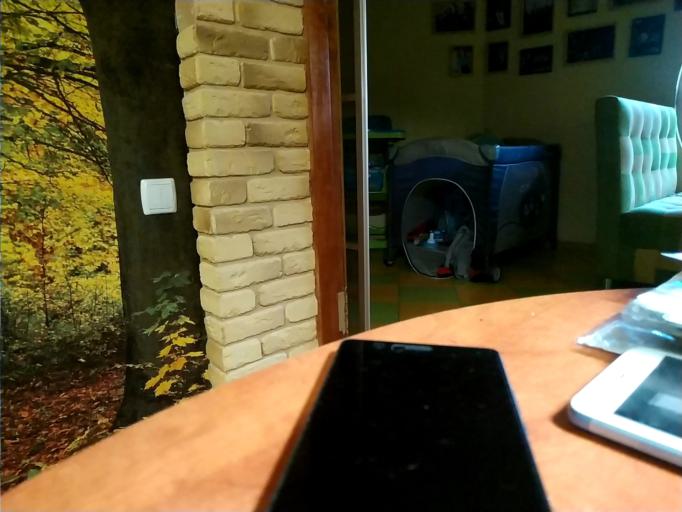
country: RU
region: Orjol
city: Znamenskoye
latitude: 53.5044
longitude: 35.5057
